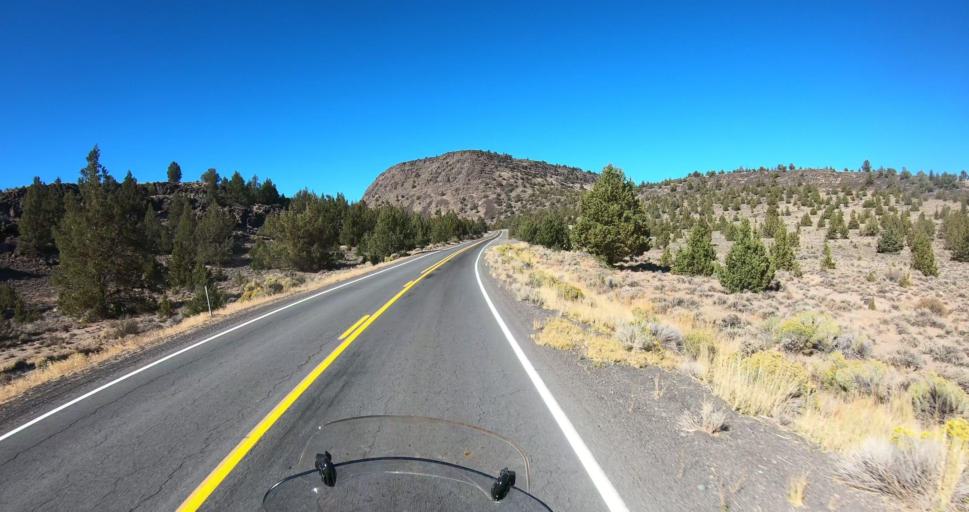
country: US
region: Oregon
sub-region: Deschutes County
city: La Pine
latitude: 43.0404
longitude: -120.7953
